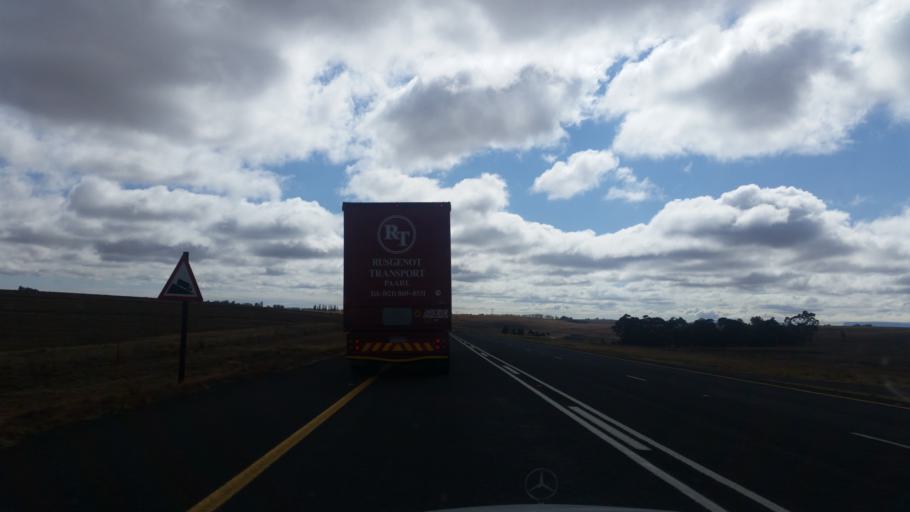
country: ZA
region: Orange Free State
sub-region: Thabo Mofutsanyana District Municipality
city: Phuthaditjhaba
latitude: -28.2743
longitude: 28.8480
